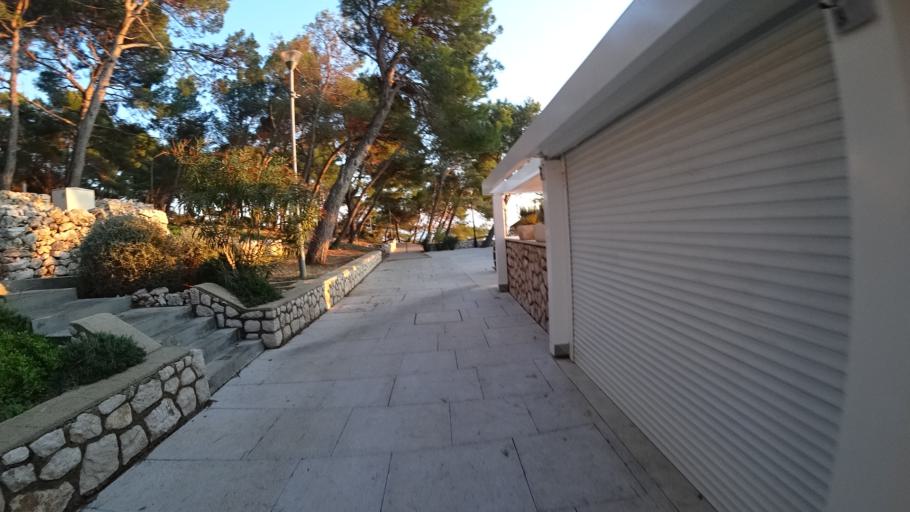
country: HR
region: Primorsko-Goranska
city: Mali Losinj
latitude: 44.5260
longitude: 14.4487
